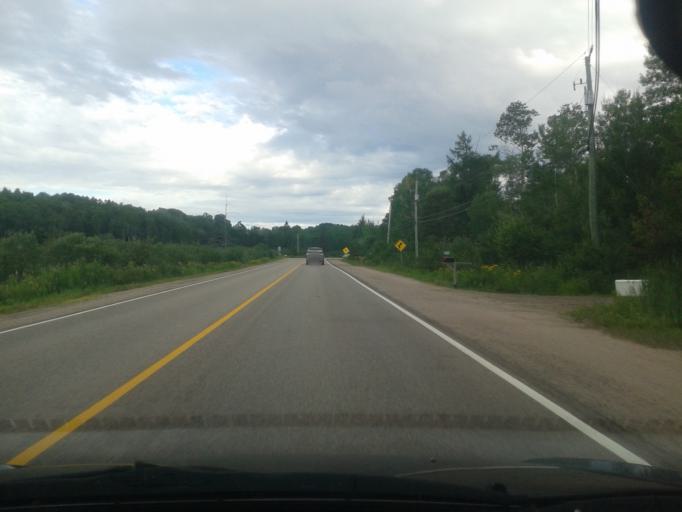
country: CA
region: Ontario
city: Powassan
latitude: 46.1902
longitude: -79.3115
